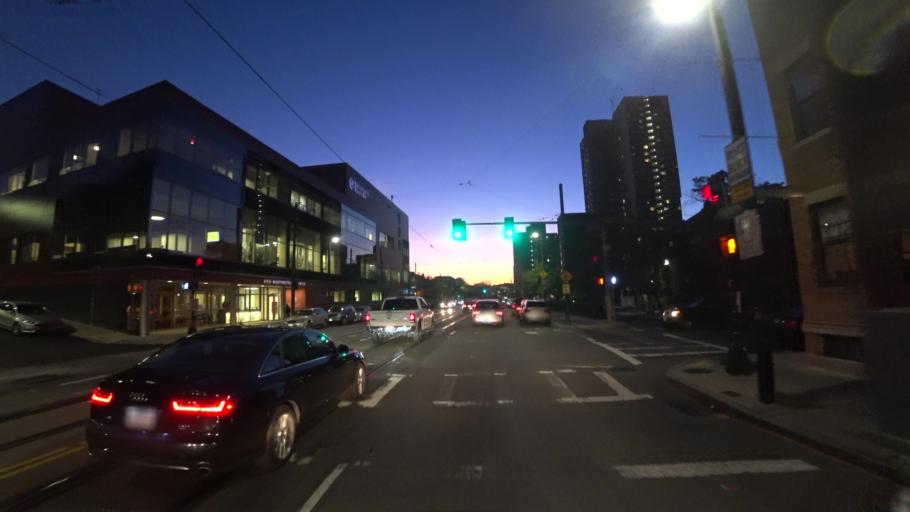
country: US
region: Massachusetts
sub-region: Norfolk County
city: Brookline
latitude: 42.3333
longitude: -71.1069
